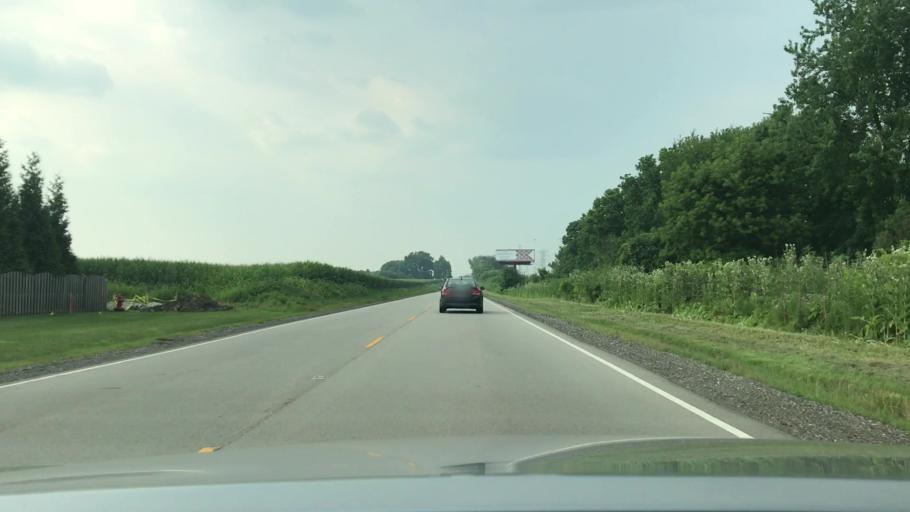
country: US
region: Illinois
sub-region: Will County
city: Plainfield
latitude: 41.6438
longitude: -88.2252
